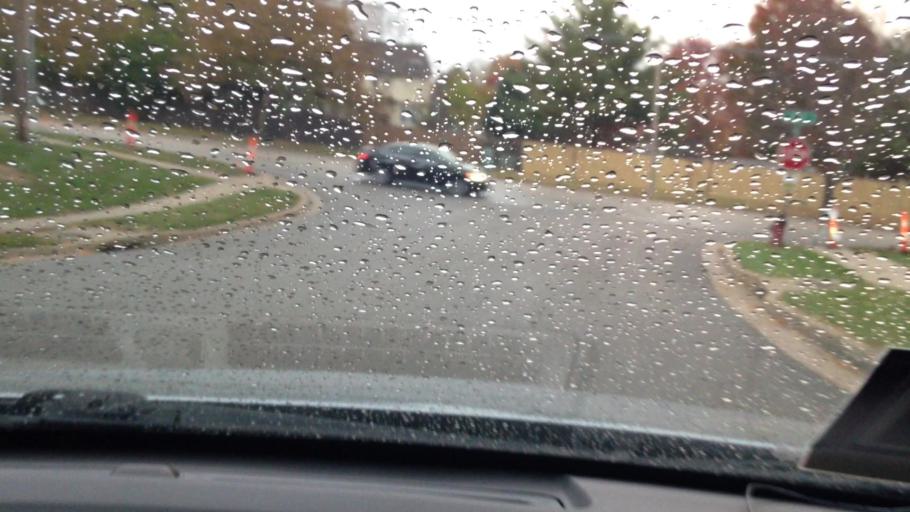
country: US
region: Missouri
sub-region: Platte County
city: Riverside
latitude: 39.2101
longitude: -94.6327
